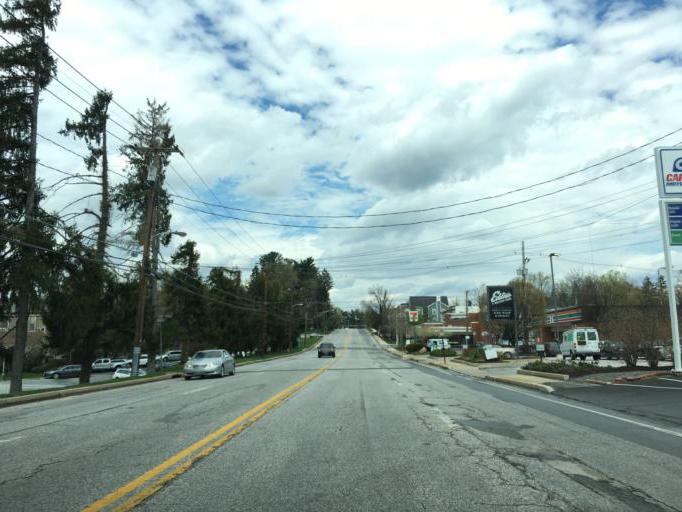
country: US
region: Maryland
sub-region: Baltimore County
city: Towson
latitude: 39.3777
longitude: -76.6269
